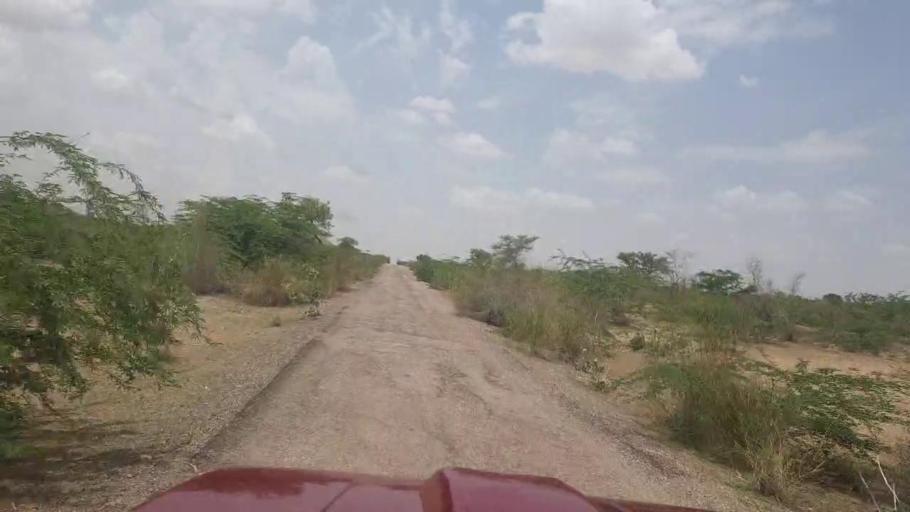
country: PK
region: Sindh
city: Islamkot
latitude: 25.2272
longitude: 70.4904
